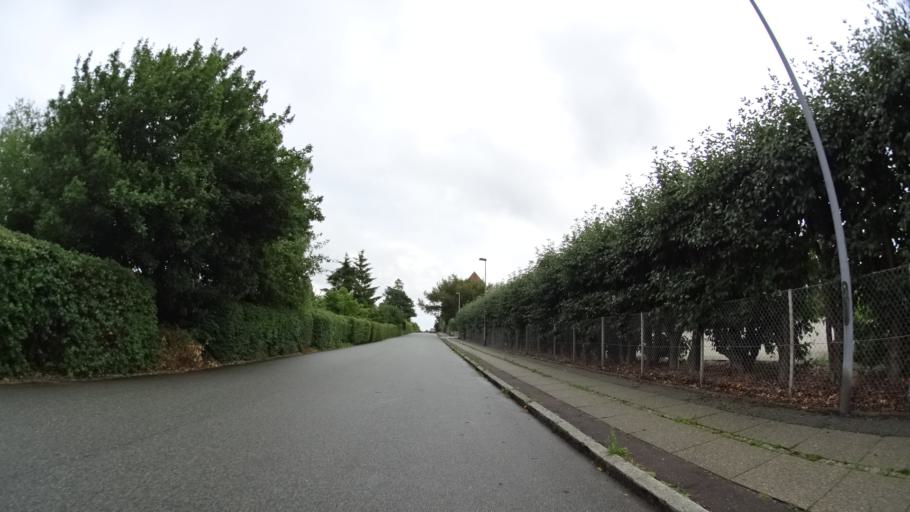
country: DK
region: Central Jutland
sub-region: Arhus Kommune
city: Arhus
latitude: 56.1260
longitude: 10.1775
